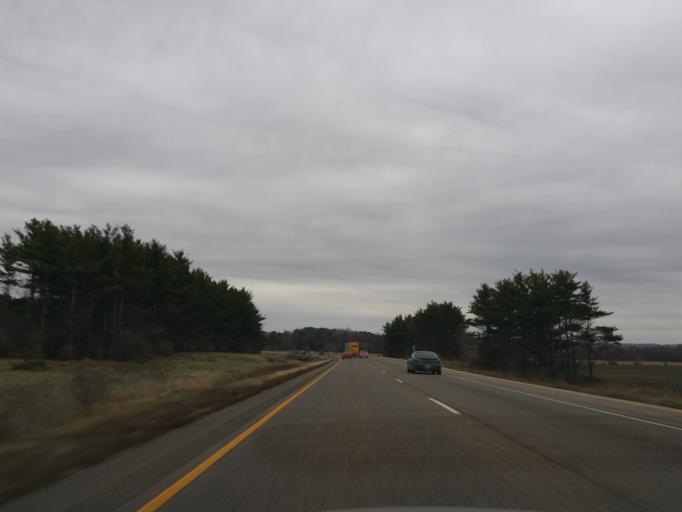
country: US
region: Wisconsin
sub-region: Saint Croix County
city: Roberts
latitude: 44.9442
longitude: -92.5312
